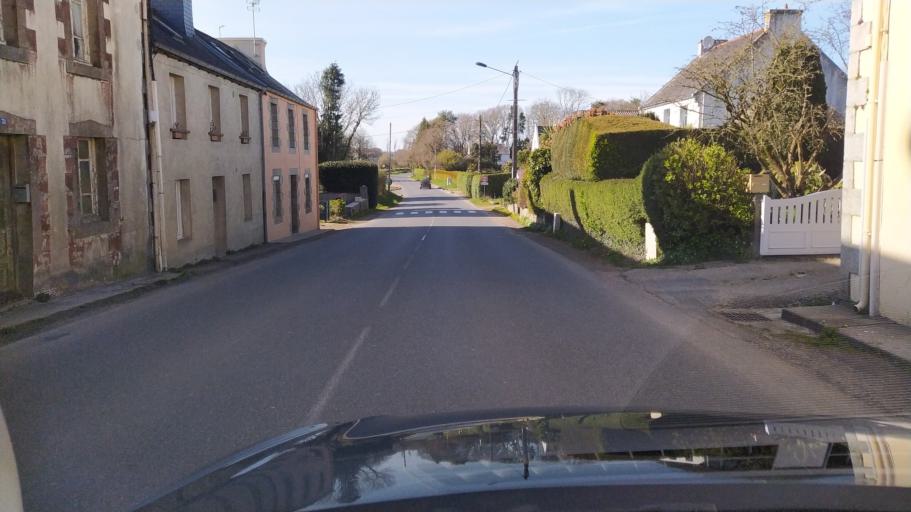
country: FR
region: Brittany
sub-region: Departement du Finistere
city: Lampaul-Guimiliau
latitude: 48.4483
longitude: -4.0067
